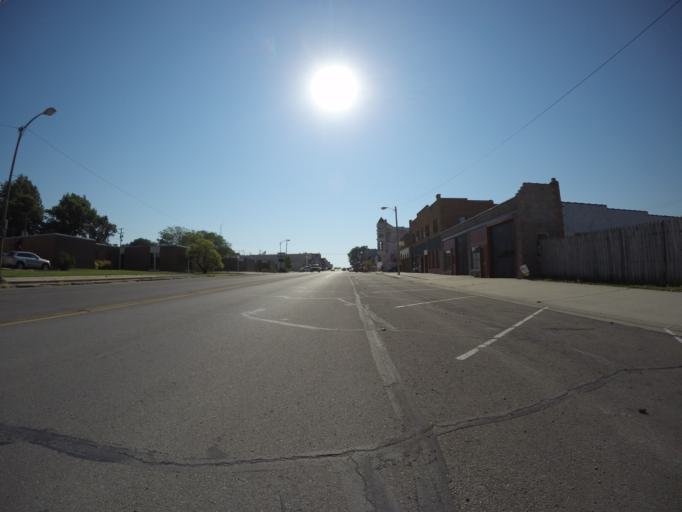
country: US
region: Kansas
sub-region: Brown County
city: Hiawatha
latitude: 39.8529
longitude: -95.5404
